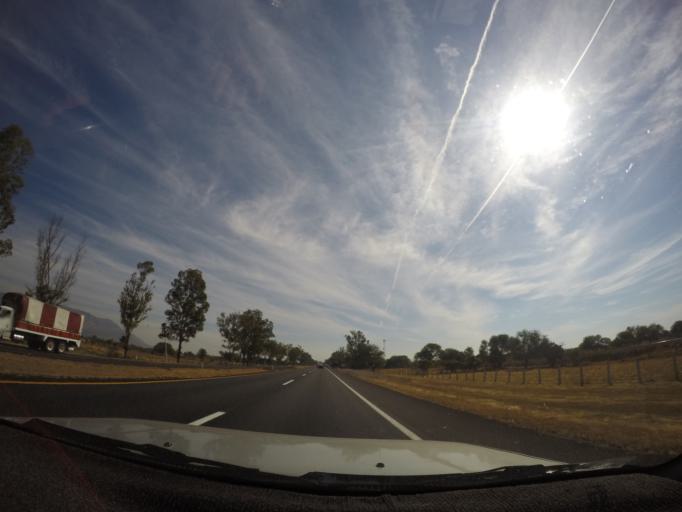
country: MX
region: Jalisco
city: Jamay
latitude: 20.3481
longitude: -102.6289
